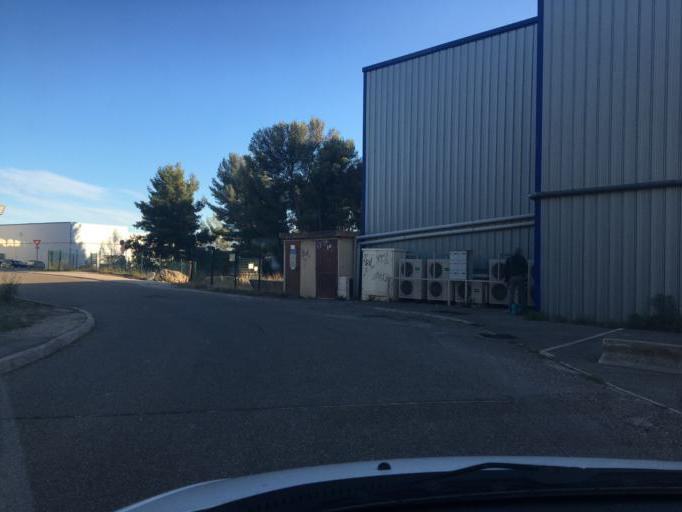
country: FR
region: Provence-Alpes-Cote d'Azur
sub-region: Departement des Bouches-du-Rhone
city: La Ciotat
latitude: 43.2020
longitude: 5.5971
